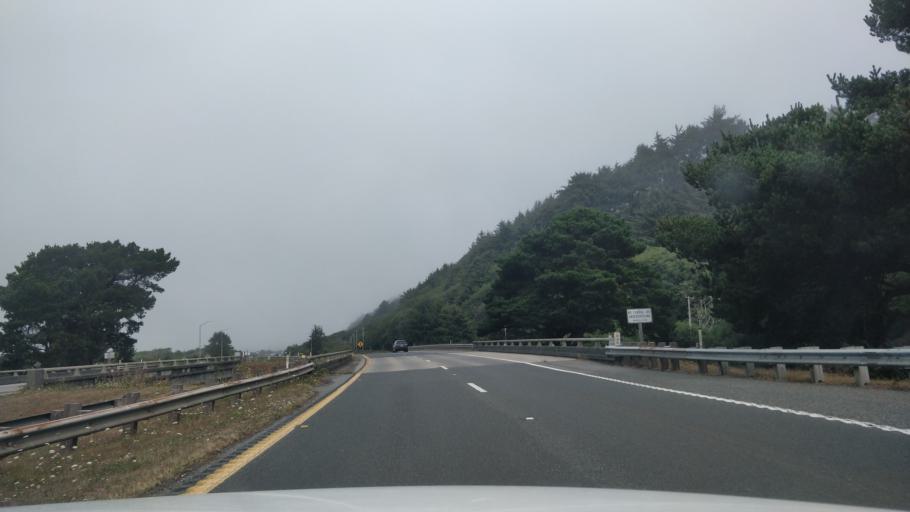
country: US
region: California
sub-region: Humboldt County
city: McKinleyville
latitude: 40.9935
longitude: -124.1135
